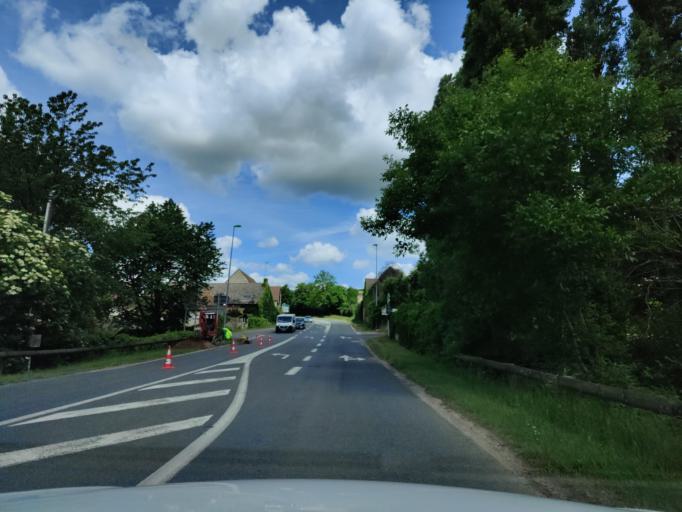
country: FR
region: Centre
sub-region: Departement du Cher
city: Saint-Amand-Montrond
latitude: 46.6689
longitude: 2.5736
